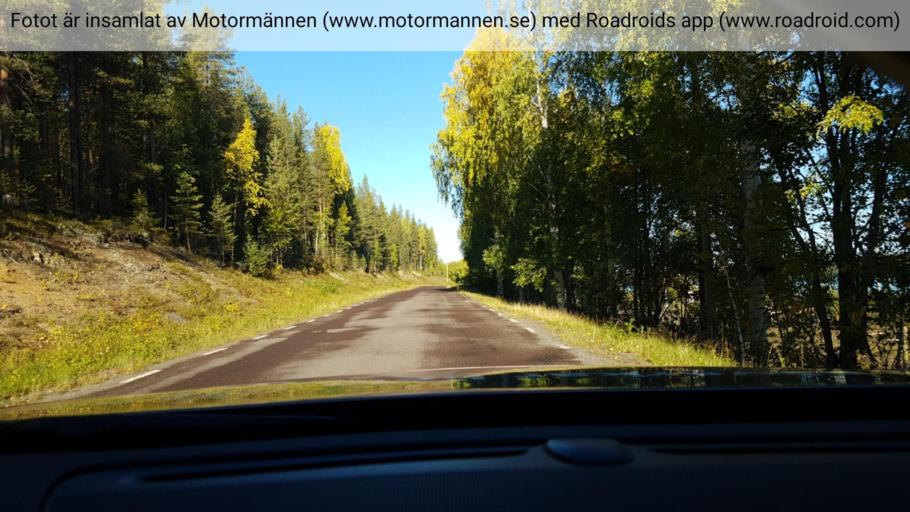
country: SE
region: Norrbotten
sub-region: Bodens Kommun
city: Boden
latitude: 66.1277
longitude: 21.3149
